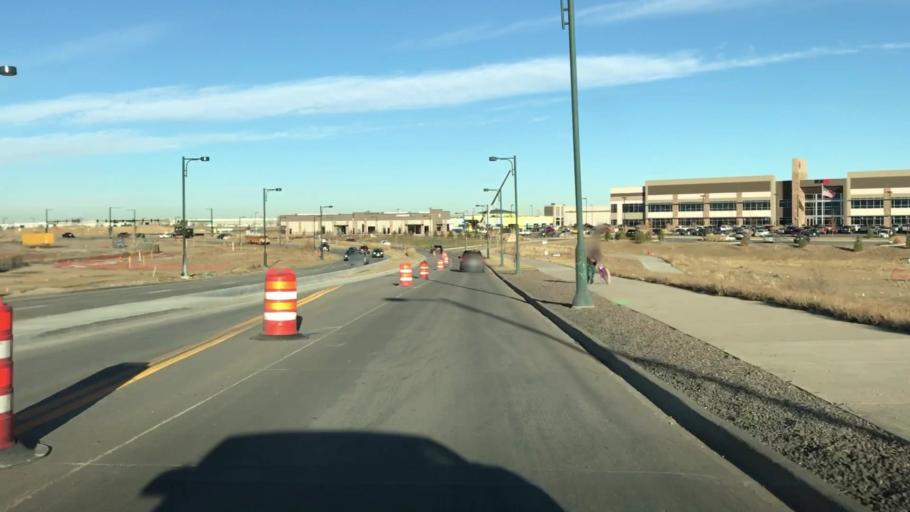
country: US
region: Colorado
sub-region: Adams County
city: Commerce City
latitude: 39.7718
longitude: -104.8852
